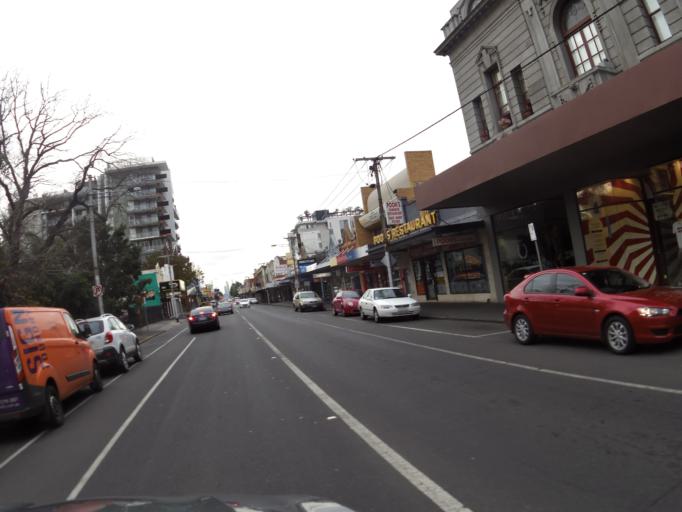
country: AU
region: Victoria
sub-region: Maribyrnong
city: Footscray
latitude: -37.7992
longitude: 144.8947
